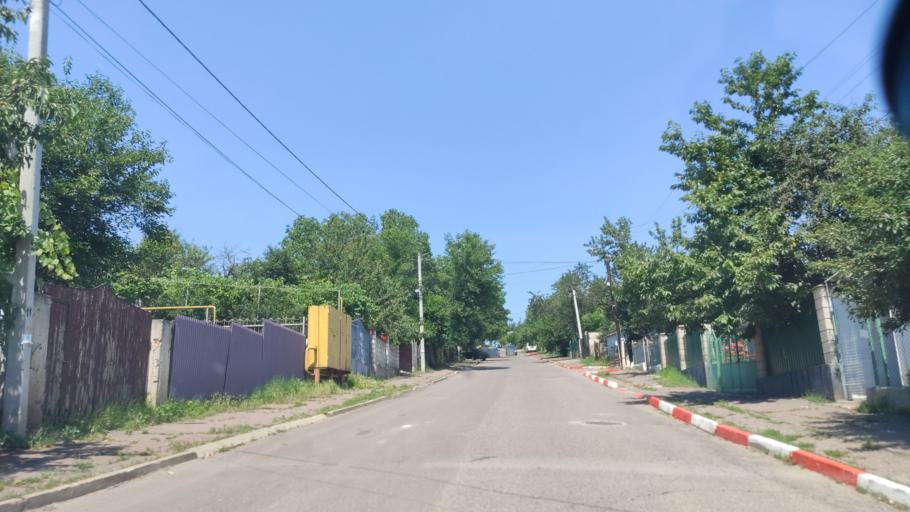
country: MD
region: Raionul Soroca
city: Soroca
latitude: 48.1711
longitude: 28.2975
